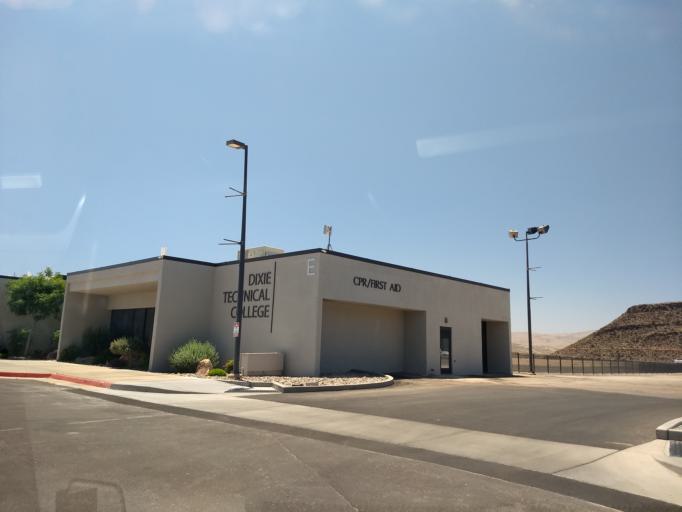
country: US
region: Utah
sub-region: Washington County
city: Saint George
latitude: 37.0979
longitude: -113.5914
